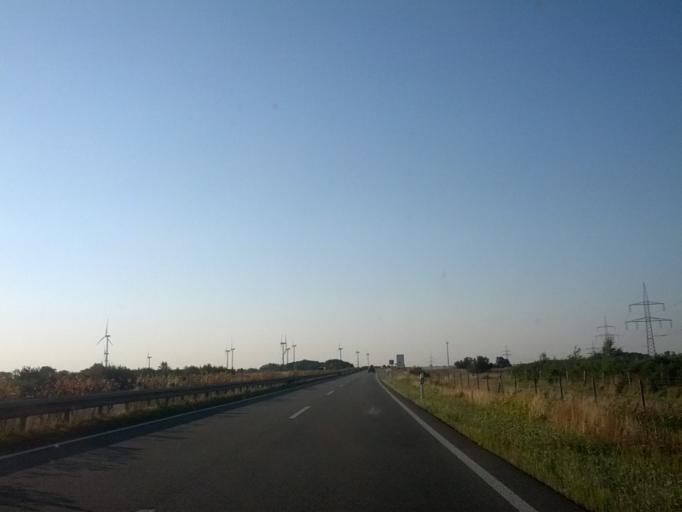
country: DE
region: Mecklenburg-Vorpommern
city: Brandshagen
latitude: 54.1821
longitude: 13.1686
